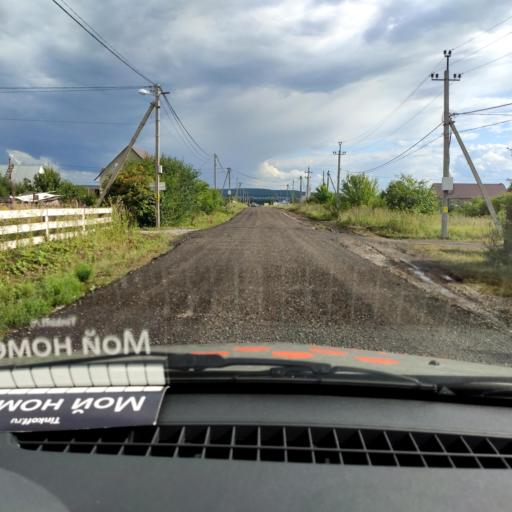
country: RU
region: Bashkortostan
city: Avdon
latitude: 54.5197
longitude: 55.8336
